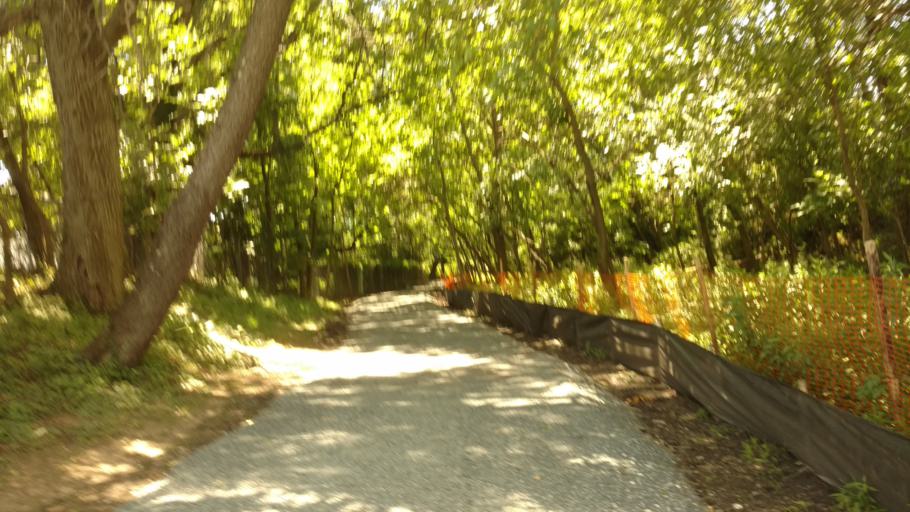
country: US
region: Maryland
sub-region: Baltimore County
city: Catonsville
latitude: 39.2668
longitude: -76.7247
